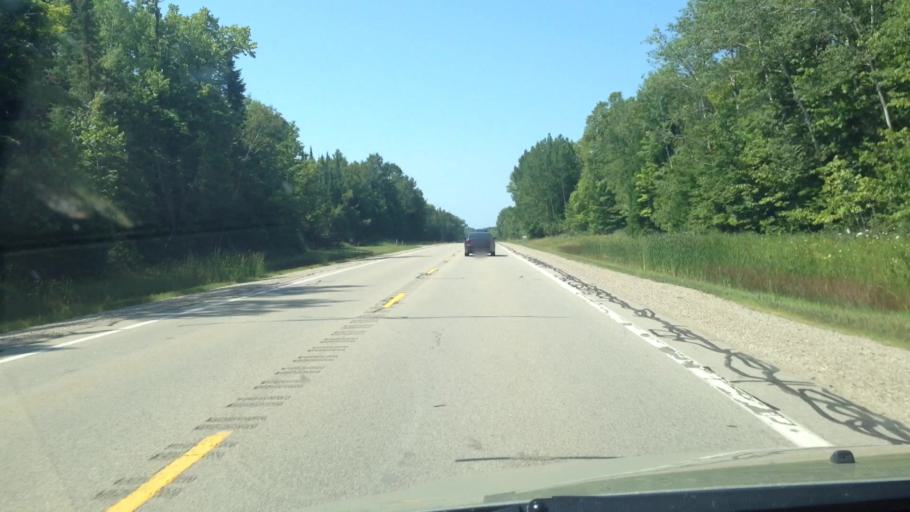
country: US
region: Michigan
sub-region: Menominee County
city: Menominee
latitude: 45.3439
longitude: -87.4117
